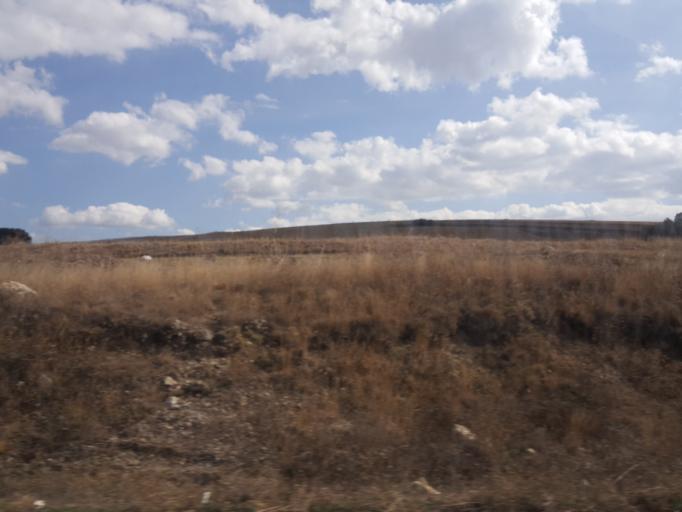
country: TR
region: Tokat
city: Artova
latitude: 40.1216
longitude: 36.3168
